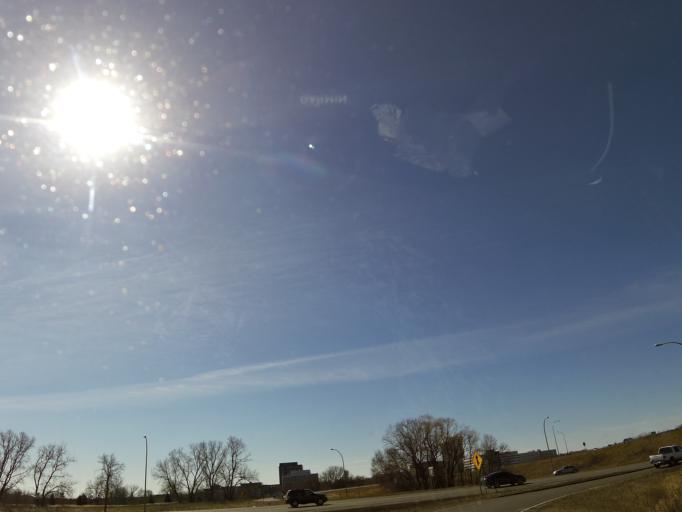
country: US
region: Minnesota
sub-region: Hennepin County
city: New Hope
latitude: 44.9840
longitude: -93.3991
